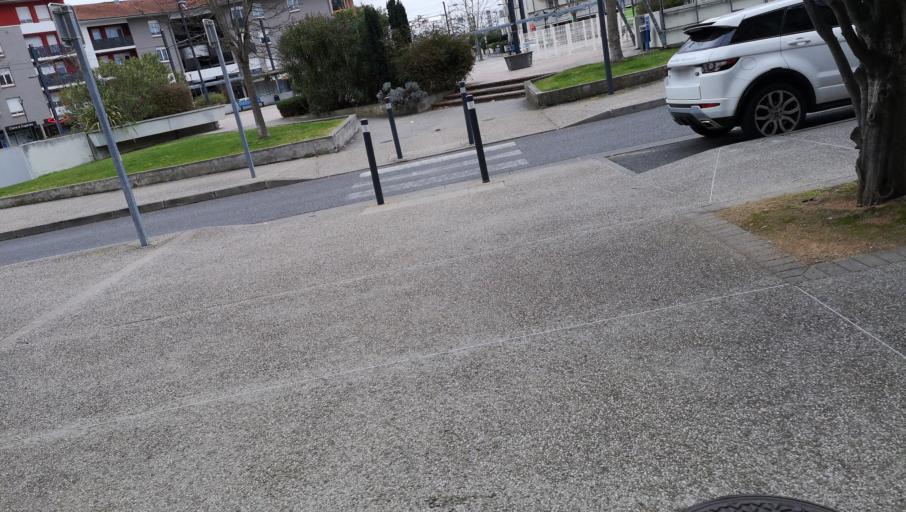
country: FR
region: Midi-Pyrenees
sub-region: Departement de la Haute-Garonne
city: Blagnac
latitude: 43.6417
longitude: 1.3792
